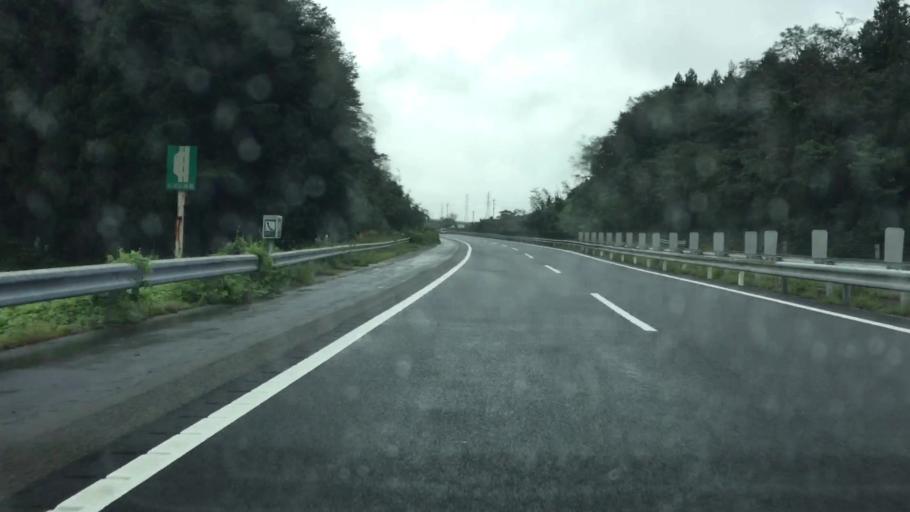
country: JP
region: Yamanashi
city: Otsuki
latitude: 35.5123
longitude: 138.8375
